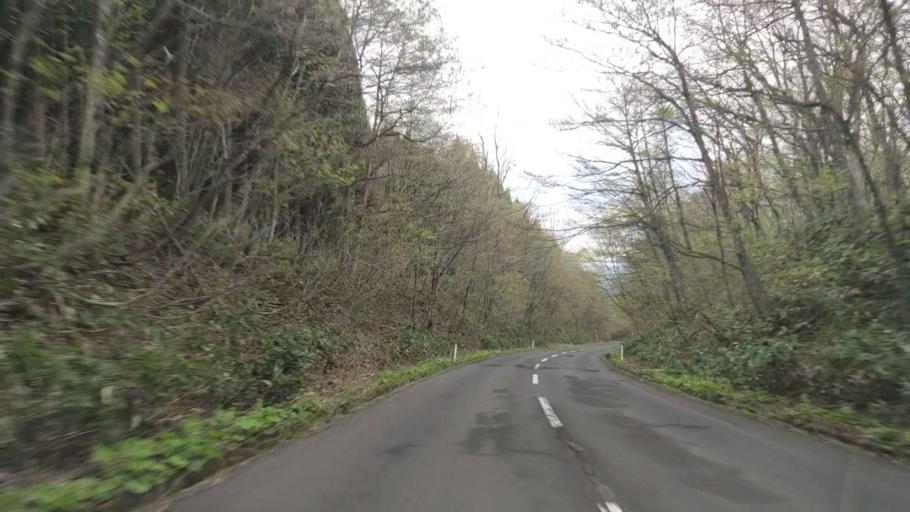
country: JP
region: Akita
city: Hanawa
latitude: 40.3843
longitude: 140.7923
